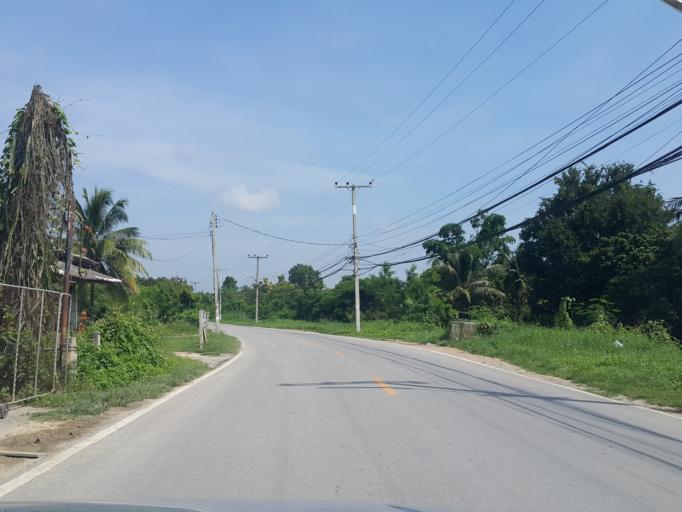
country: TH
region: Chiang Mai
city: Saraphi
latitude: 18.6881
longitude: 99.0607
